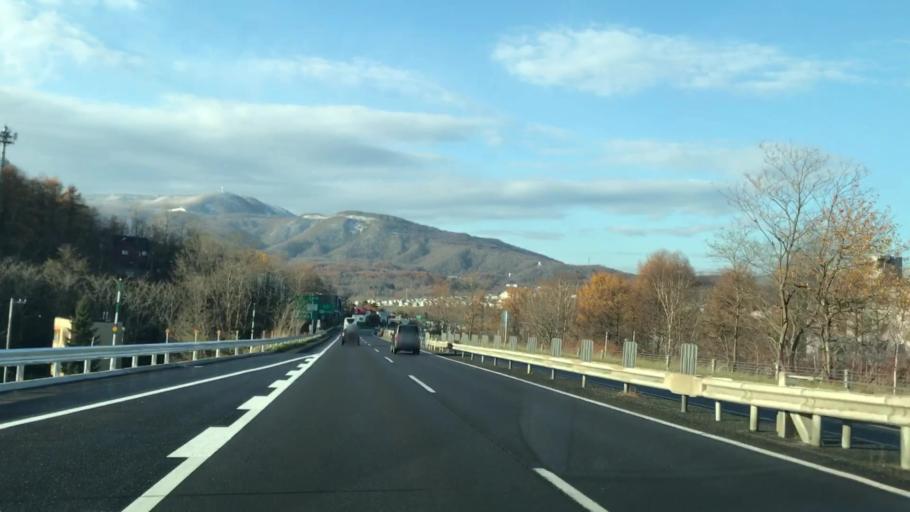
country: JP
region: Hokkaido
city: Otaru
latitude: 43.1701
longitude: 141.0616
